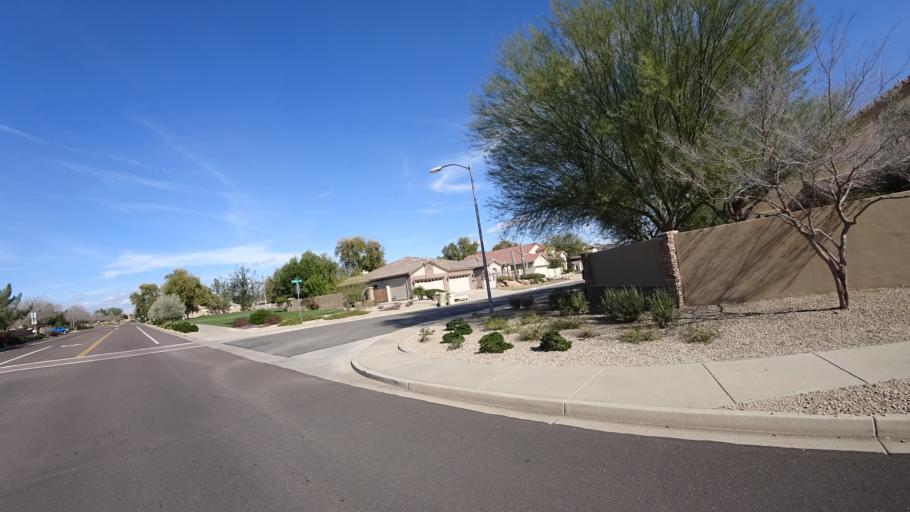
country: US
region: Arizona
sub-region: Maricopa County
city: Sun City
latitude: 33.6783
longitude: -112.2125
